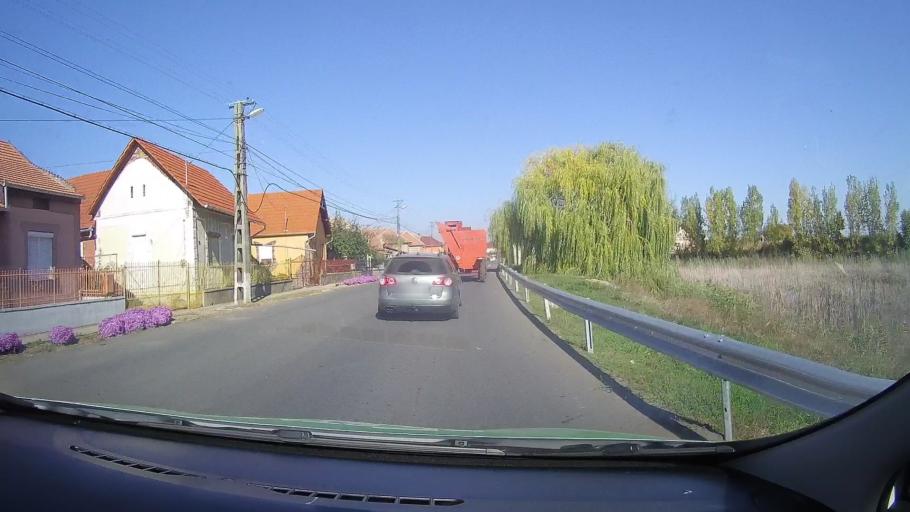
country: RO
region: Satu Mare
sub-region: Comuna Berveni
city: Lucaceni
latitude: 47.7350
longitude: 22.4754
